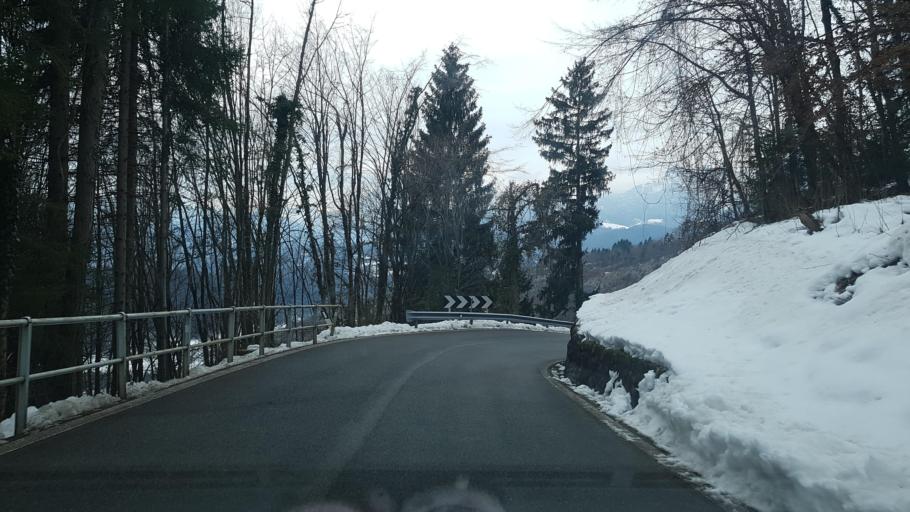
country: IT
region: Friuli Venezia Giulia
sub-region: Provincia di Udine
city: Lauco
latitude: 46.4244
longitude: 12.9235
